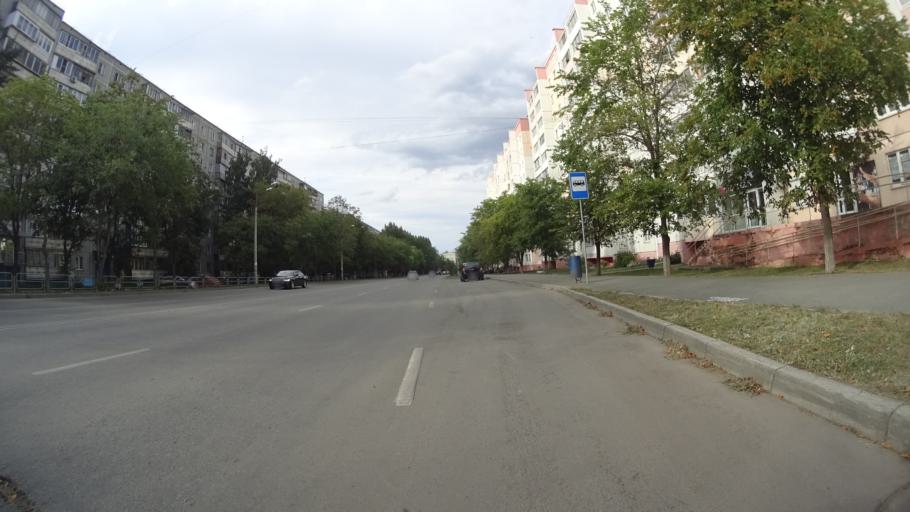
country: RU
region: Chelyabinsk
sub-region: Gorod Chelyabinsk
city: Chelyabinsk
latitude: 55.1958
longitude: 61.3179
